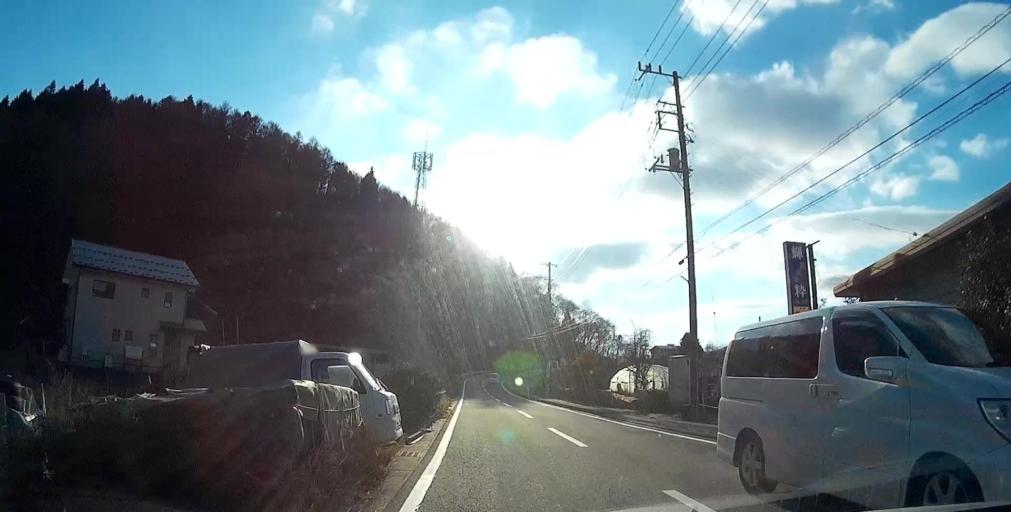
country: JP
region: Yamanashi
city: Fujikawaguchiko
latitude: 35.4912
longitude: 138.8231
